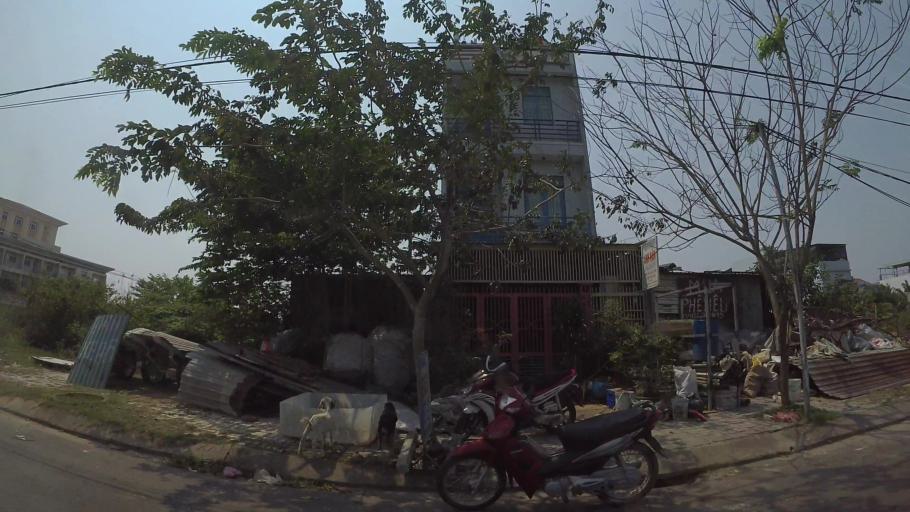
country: VN
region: Da Nang
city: Cam Le
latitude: 15.9830
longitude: 108.2113
